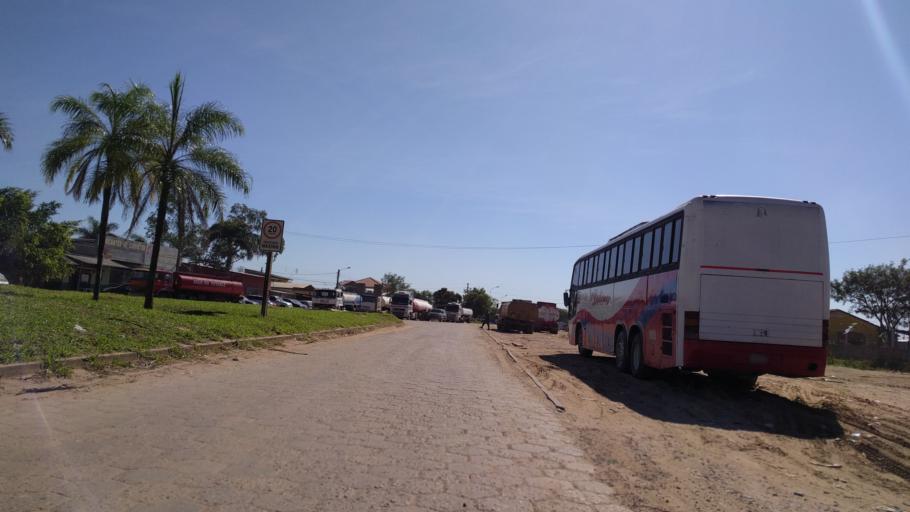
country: BO
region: Santa Cruz
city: Santa Cruz de la Sierra
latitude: -17.8752
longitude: -63.1935
